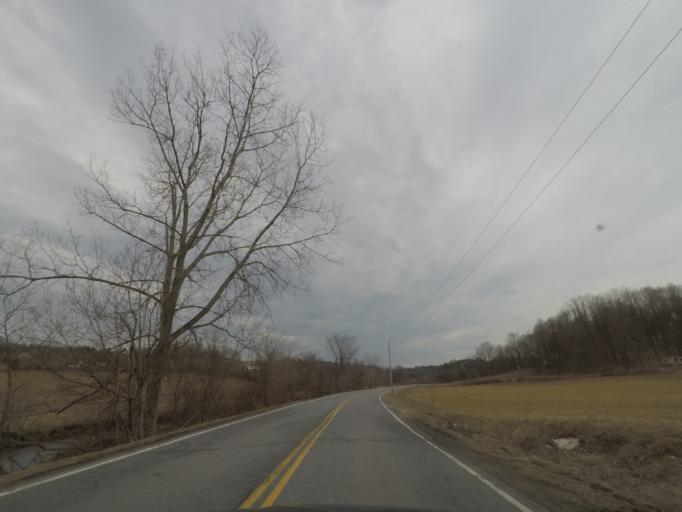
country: US
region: New York
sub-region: Washington County
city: Greenwich
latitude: 43.0751
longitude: -73.4953
